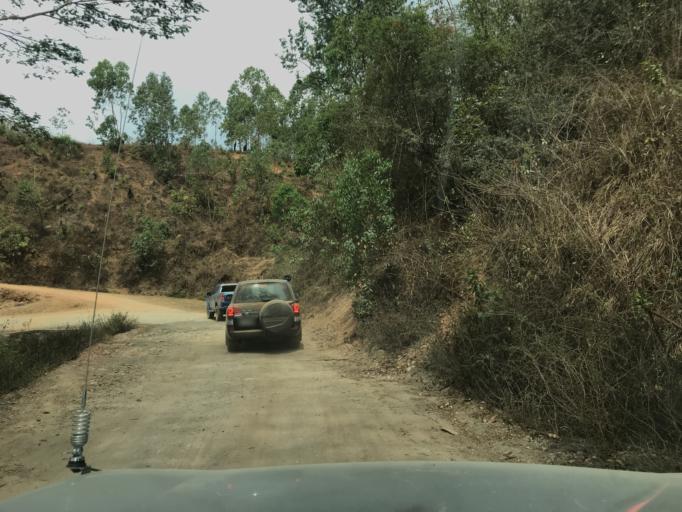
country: TL
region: Ermera
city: Gleno
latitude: -8.8256
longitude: 125.4358
